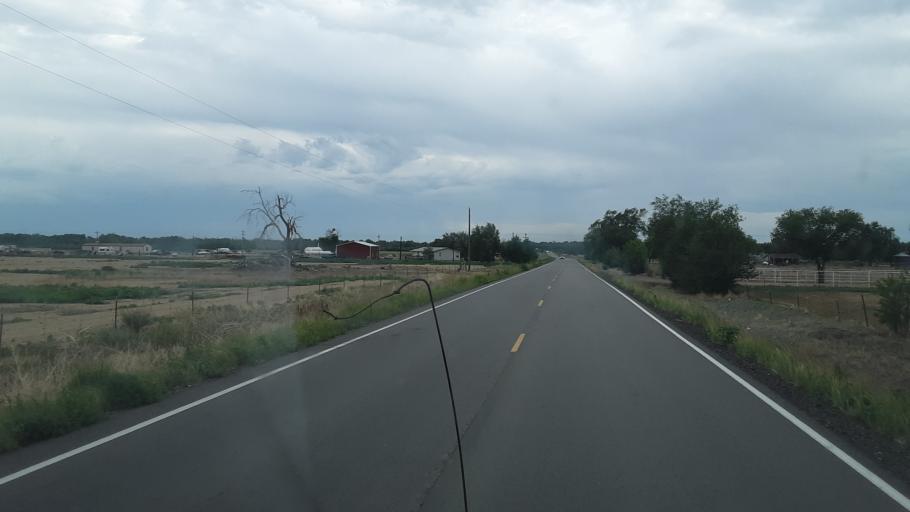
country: US
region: Colorado
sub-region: Otero County
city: Fowler
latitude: 38.1514
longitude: -104.0232
